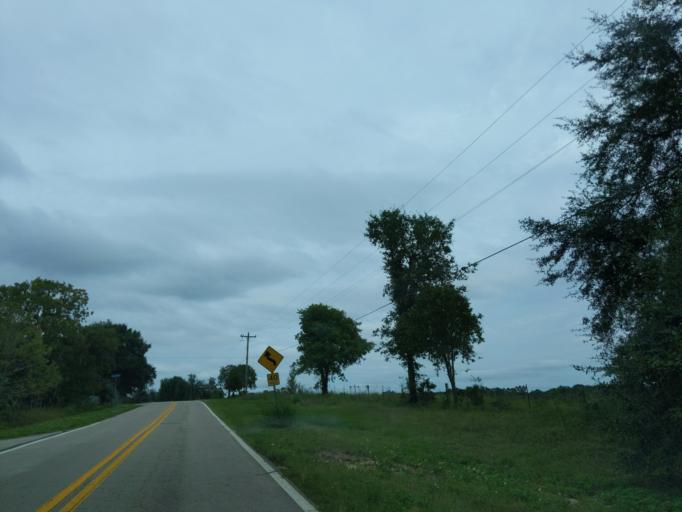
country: US
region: Florida
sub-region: Gadsden County
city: Midway
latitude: 30.4348
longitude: -84.4121
